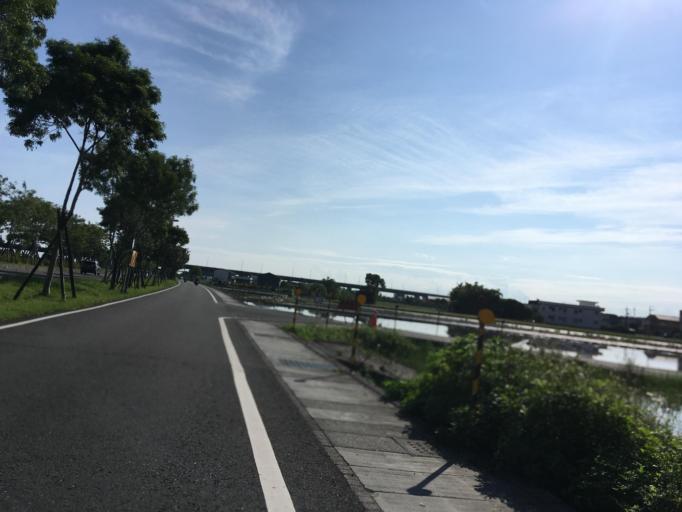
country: TW
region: Taiwan
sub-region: Yilan
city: Yilan
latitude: 24.6791
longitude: 121.7884
